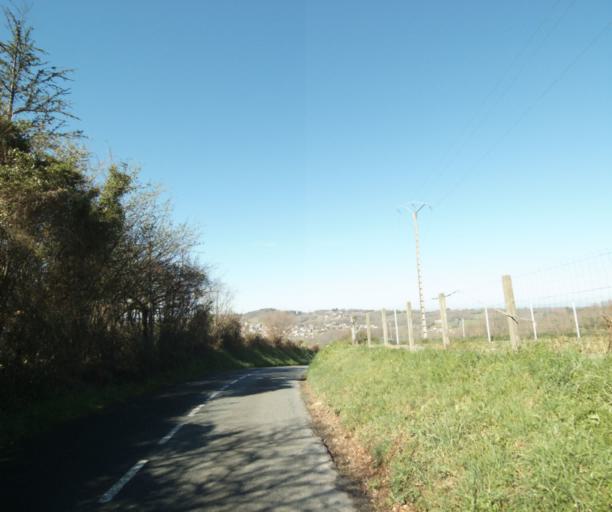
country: FR
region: Aquitaine
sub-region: Departement des Pyrenees-Atlantiques
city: Urrugne
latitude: 43.3615
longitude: -1.6842
